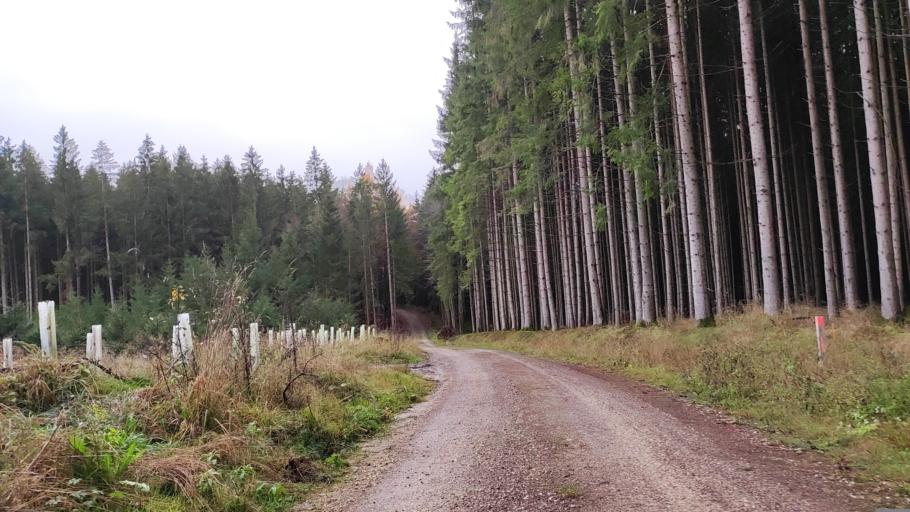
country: DE
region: Bavaria
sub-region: Swabia
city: Burtenbach
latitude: 48.3638
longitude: 10.5176
